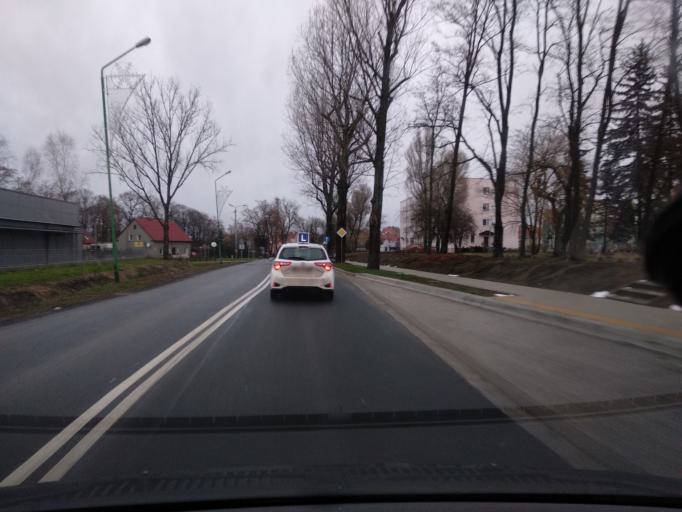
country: PL
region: Lower Silesian Voivodeship
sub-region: Powiat polkowicki
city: Polkowice
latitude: 51.4988
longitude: 16.0692
